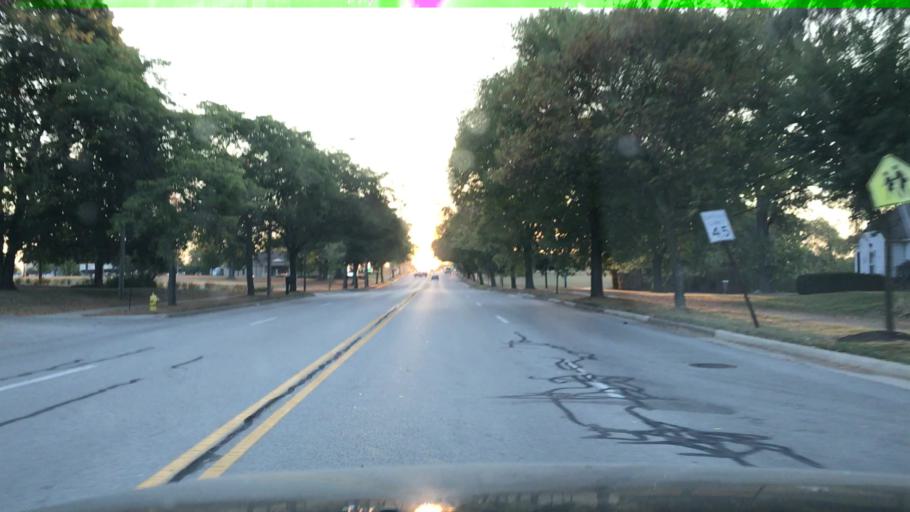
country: US
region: Michigan
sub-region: Kent County
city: East Grand Rapids
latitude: 42.9843
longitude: -85.5960
